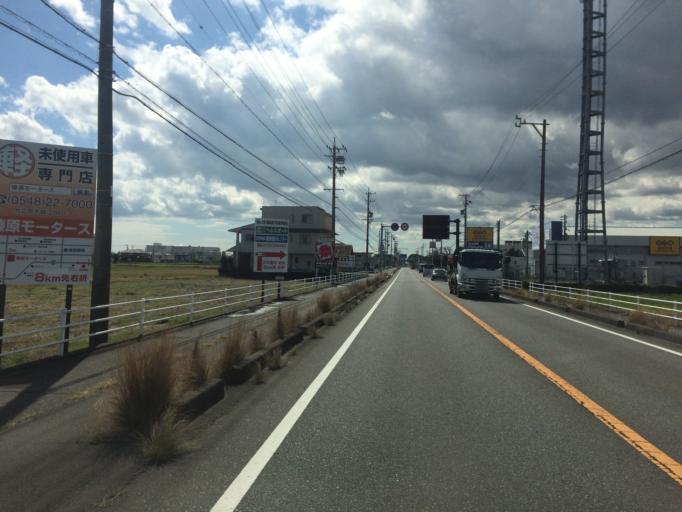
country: JP
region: Shizuoka
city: Fujieda
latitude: 34.8079
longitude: 138.2699
